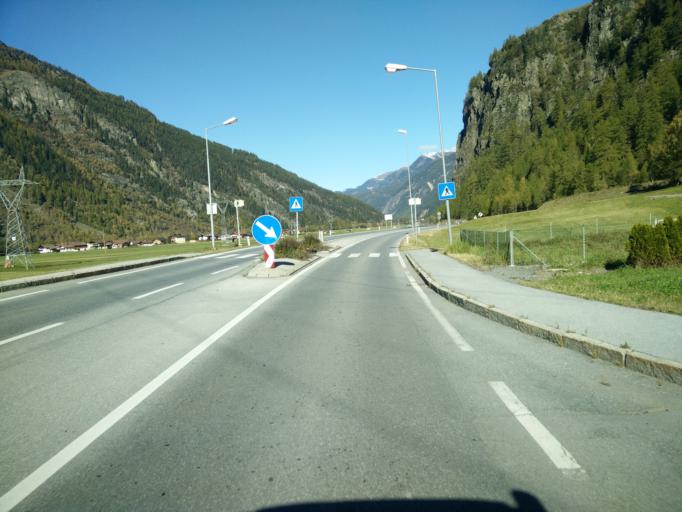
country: AT
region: Tyrol
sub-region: Politischer Bezirk Imst
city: Umhausen
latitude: 47.0507
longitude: 10.9660
